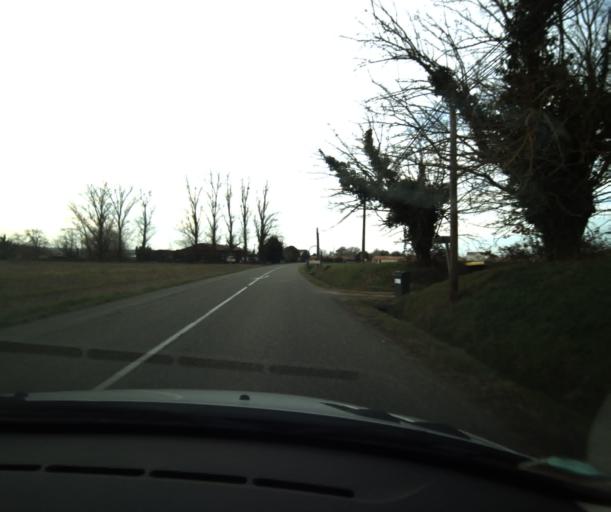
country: FR
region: Midi-Pyrenees
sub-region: Departement du Tarn-et-Garonne
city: Montech
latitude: 43.9398
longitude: 1.2409
